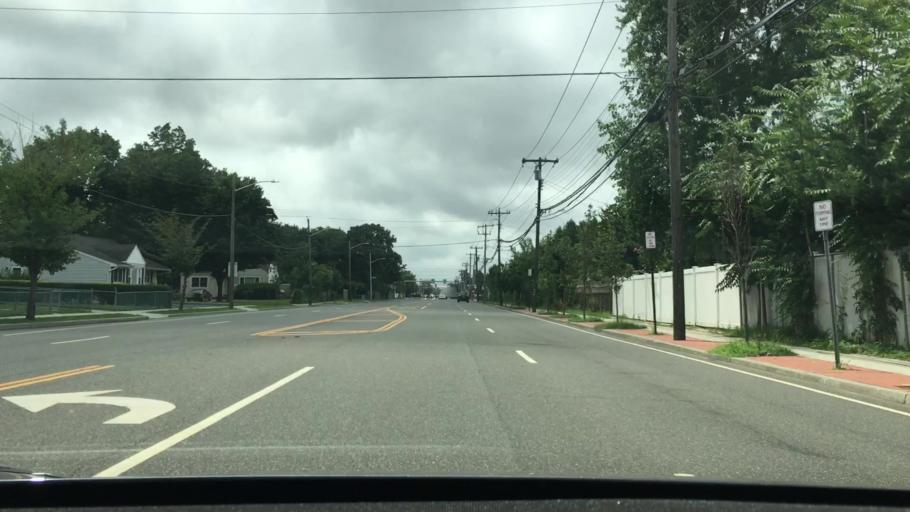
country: US
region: New York
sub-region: Nassau County
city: Hicksville
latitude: 40.7736
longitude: -73.5019
